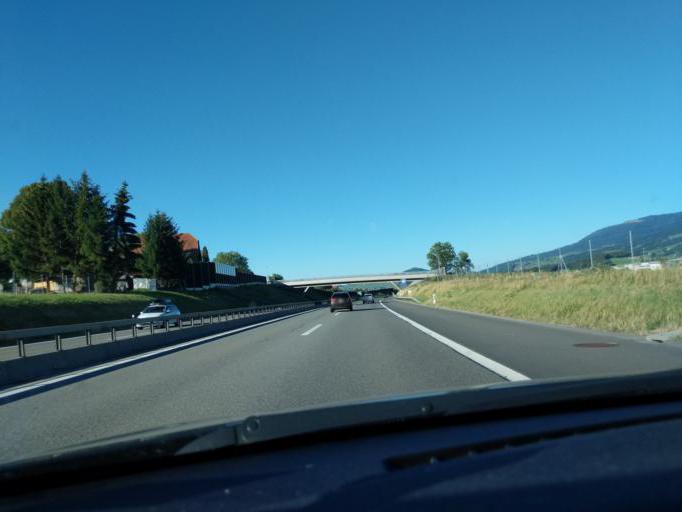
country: CH
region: Fribourg
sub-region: Gruyere District
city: Riaz
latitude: 46.6399
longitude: 7.0515
